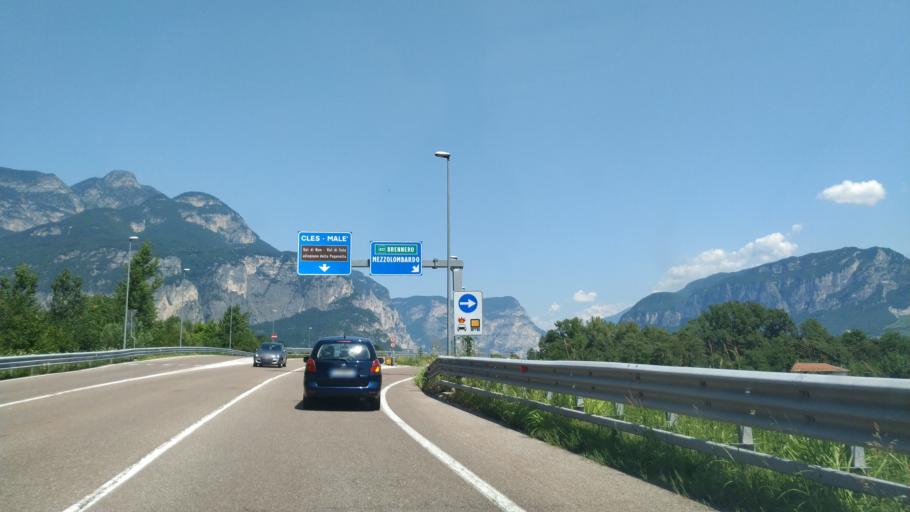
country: IT
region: Trentino-Alto Adige
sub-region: Provincia di Trento
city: Nave San Rocco
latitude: 46.1860
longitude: 11.0992
